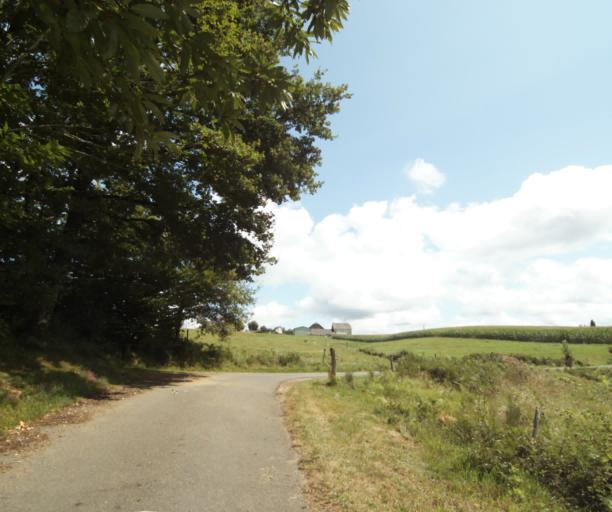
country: FR
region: Limousin
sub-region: Departement de la Correze
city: Sainte-Fortunade
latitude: 45.2128
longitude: 1.8062
